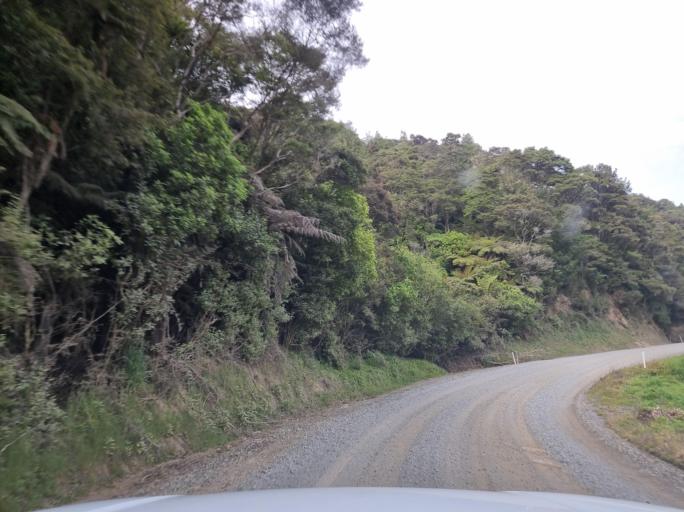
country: NZ
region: Northland
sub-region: Whangarei
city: Ruakaka
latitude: -36.0448
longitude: 174.4108
